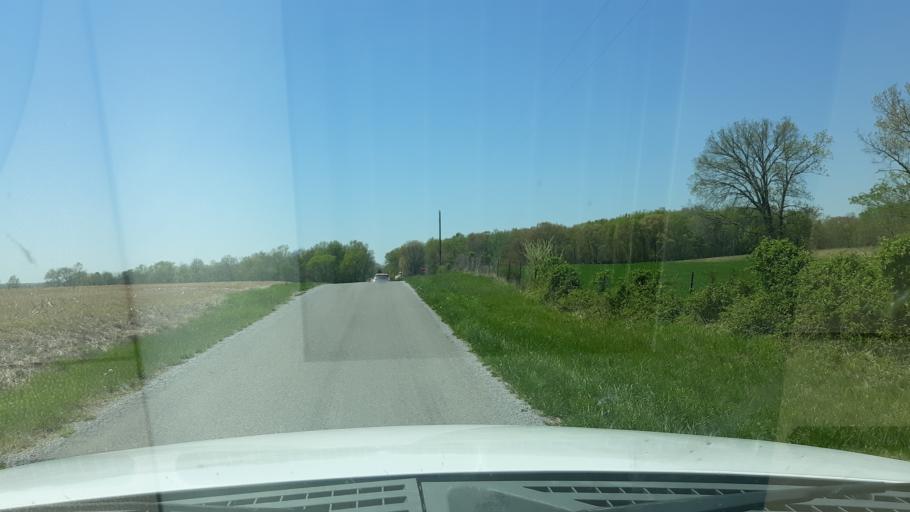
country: US
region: Illinois
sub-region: Saline County
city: Harrisburg
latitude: 37.8849
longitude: -88.6501
